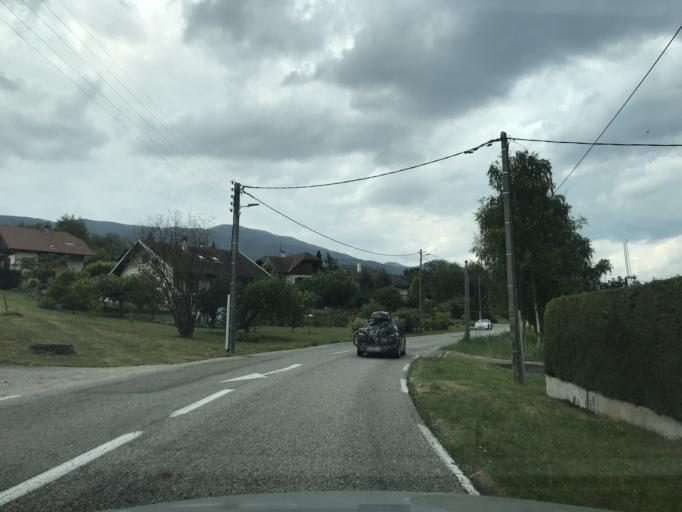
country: FR
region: Rhone-Alpes
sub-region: Departement de la Savoie
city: Brison-Saint-Innocent
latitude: 45.7325
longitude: 5.8875
